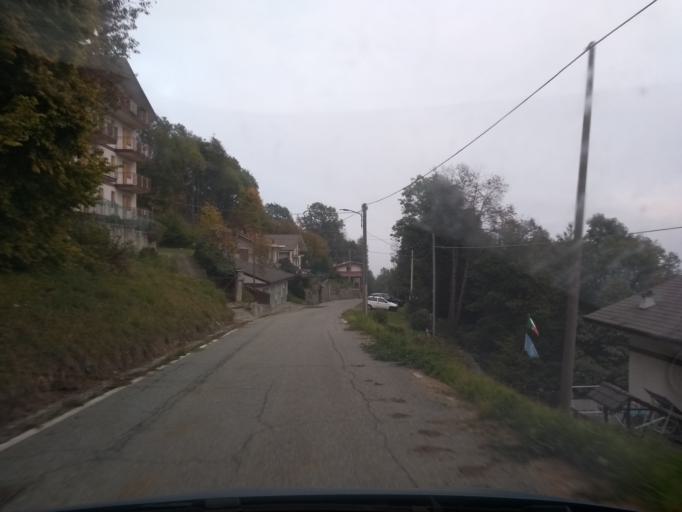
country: IT
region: Piedmont
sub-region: Provincia di Torino
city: Pessinetto
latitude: 45.3029
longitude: 7.4159
